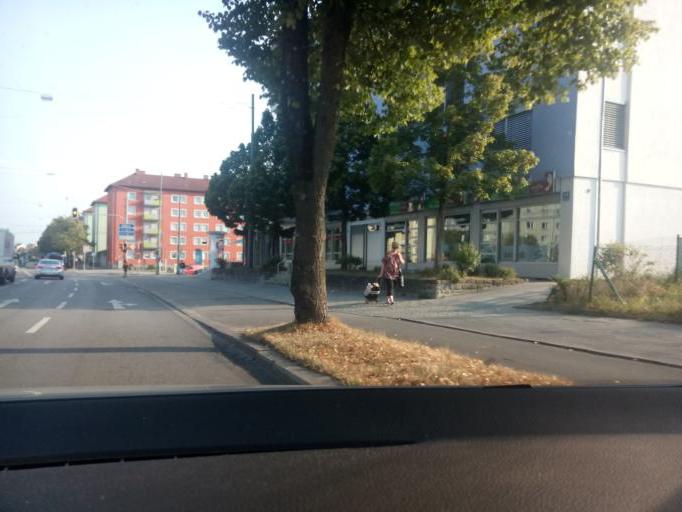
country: DE
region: Bavaria
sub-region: Upper Bavaria
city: Munich
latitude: 48.1055
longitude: 11.5970
